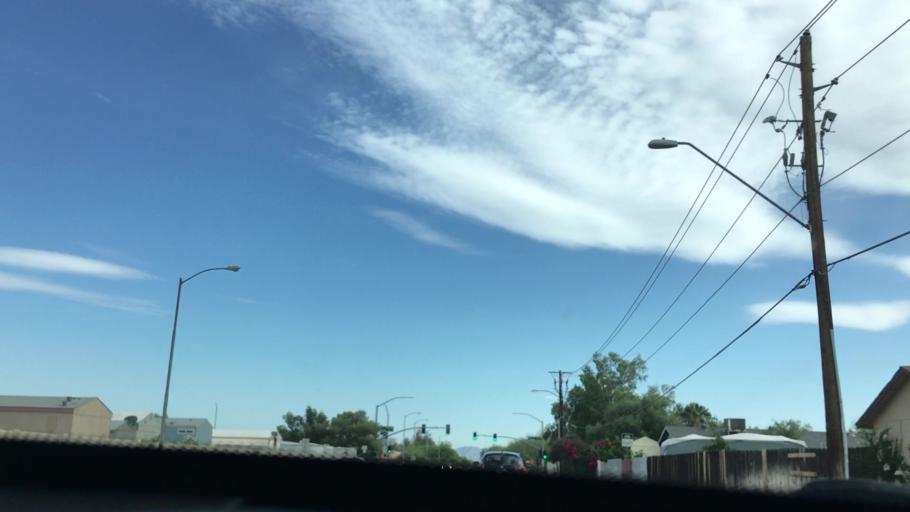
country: US
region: Arizona
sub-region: Maricopa County
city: Peoria
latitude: 33.5824
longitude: -112.2290
